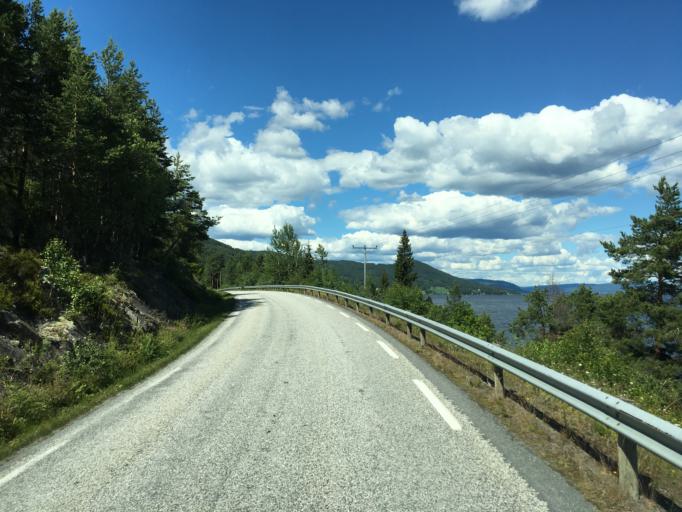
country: NO
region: Oppland
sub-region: Jevnaker
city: Jevnaker
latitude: 60.3043
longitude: 10.3513
